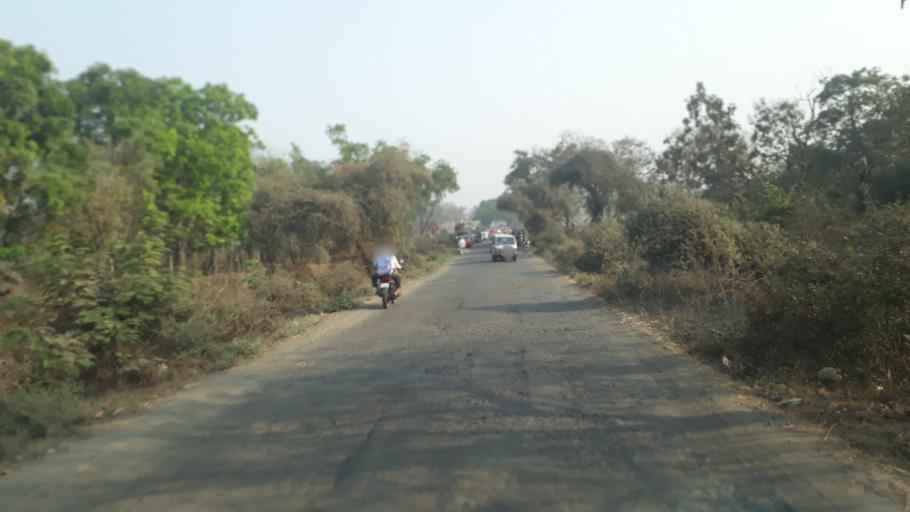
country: IN
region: Maharashtra
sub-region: Raigarh
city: Neral
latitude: 19.0416
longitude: 73.3310
